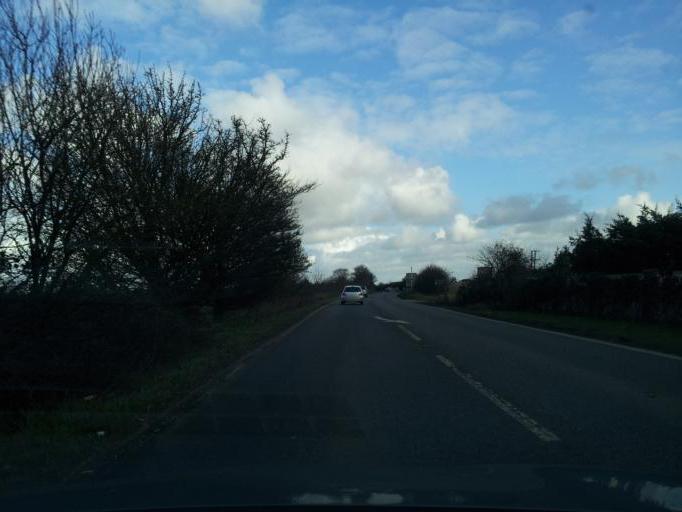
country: GB
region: England
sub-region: Norfolk
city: Diss
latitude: 52.3500
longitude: 1.1365
